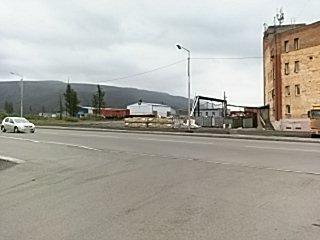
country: RU
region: Krasnoyarskiy
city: Talnakh
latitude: 69.4851
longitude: 88.3985
